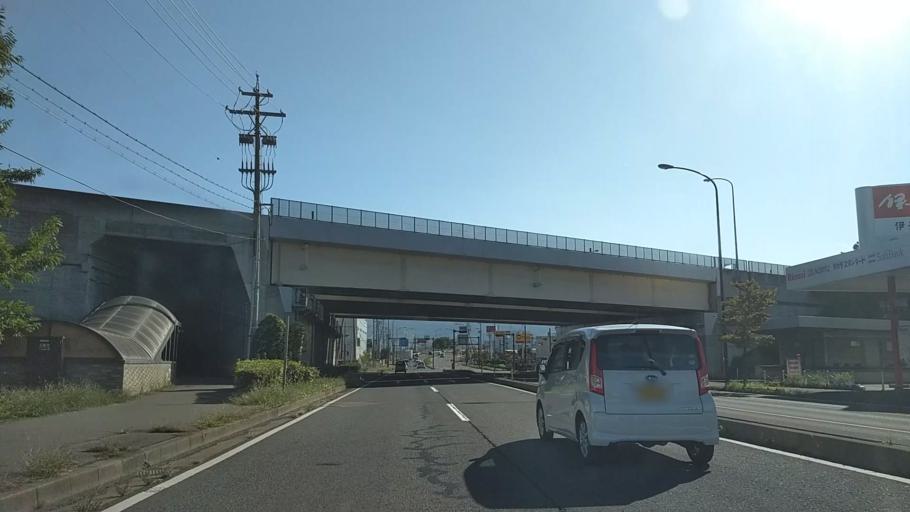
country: JP
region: Nagano
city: Nagano-shi
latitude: 36.5526
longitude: 138.1365
